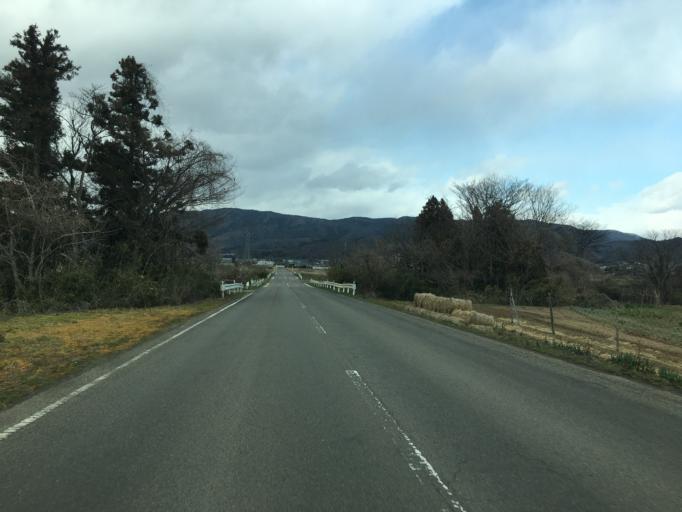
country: JP
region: Fukushima
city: Hobaramachi
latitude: 37.8614
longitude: 140.5380
